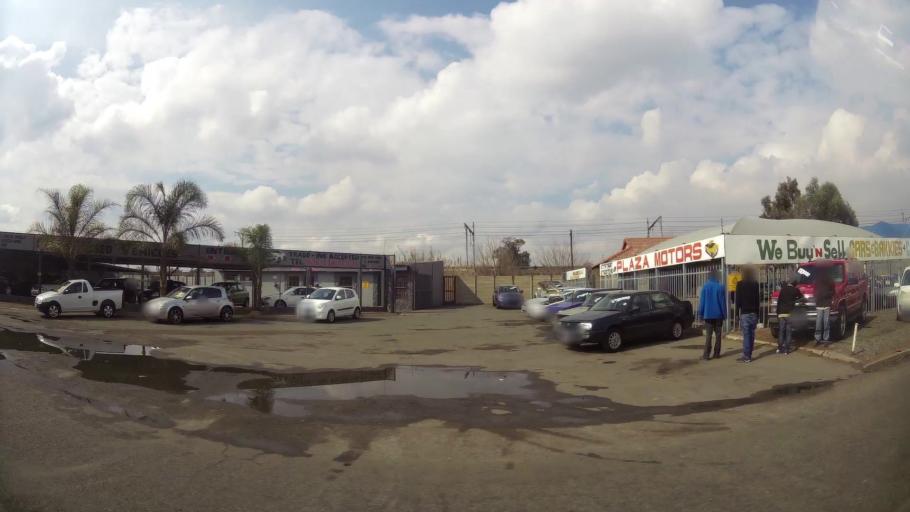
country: ZA
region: Gauteng
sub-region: Sedibeng District Municipality
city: Vereeniging
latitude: -26.6835
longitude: 27.9319
